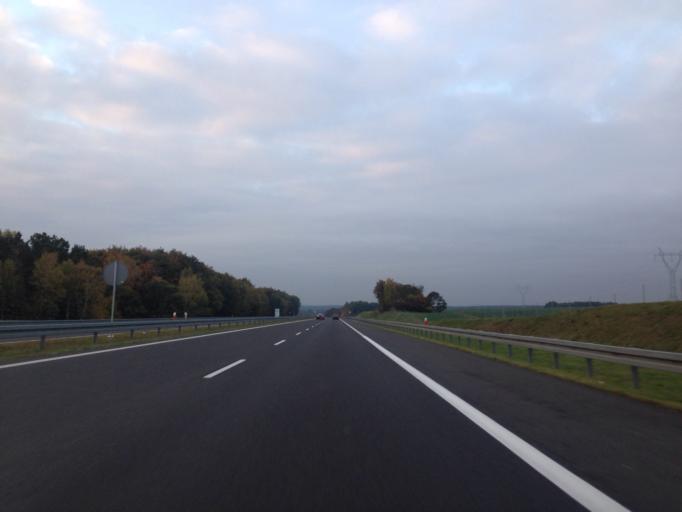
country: PL
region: Kujawsko-Pomorskie
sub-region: Powiat swiecki
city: Warlubie
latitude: 53.5393
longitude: 18.6067
